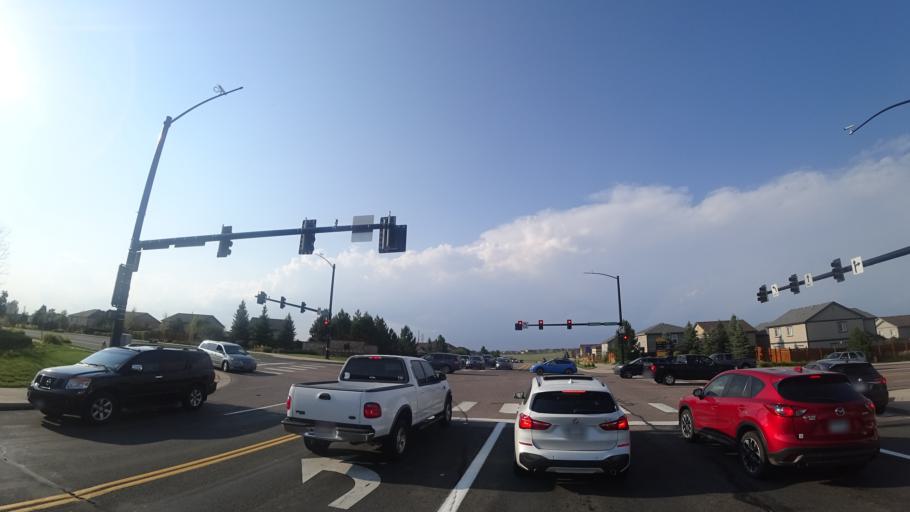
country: US
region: Colorado
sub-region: Arapahoe County
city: Dove Valley
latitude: 39.6269
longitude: -104.7382
